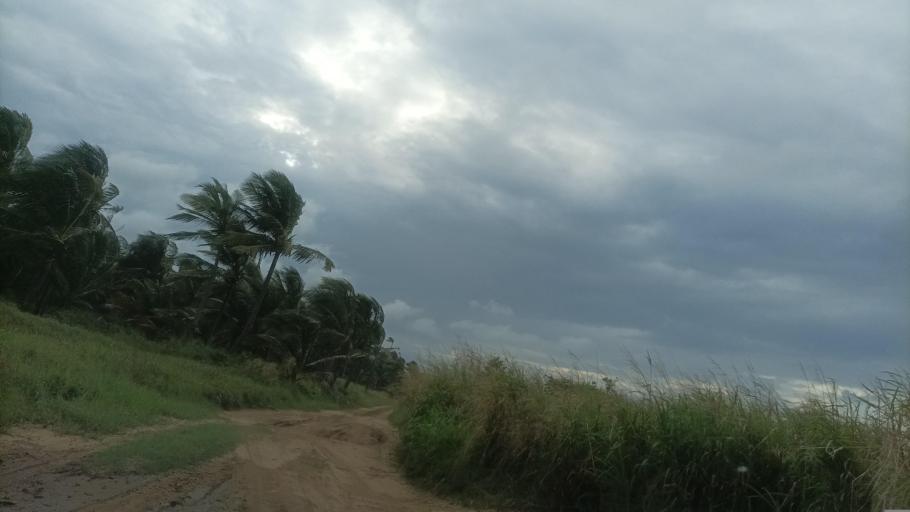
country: MX
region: Veracruz
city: Agua Dulce
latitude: 18.1819
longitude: -94.2640
